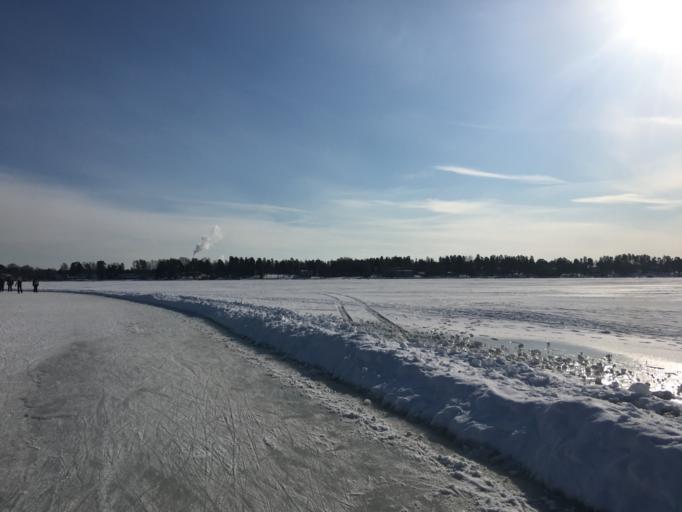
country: FI
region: Uusimaa
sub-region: Helsinki
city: Teekkarikylae
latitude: 60.1943
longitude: 24.8575
